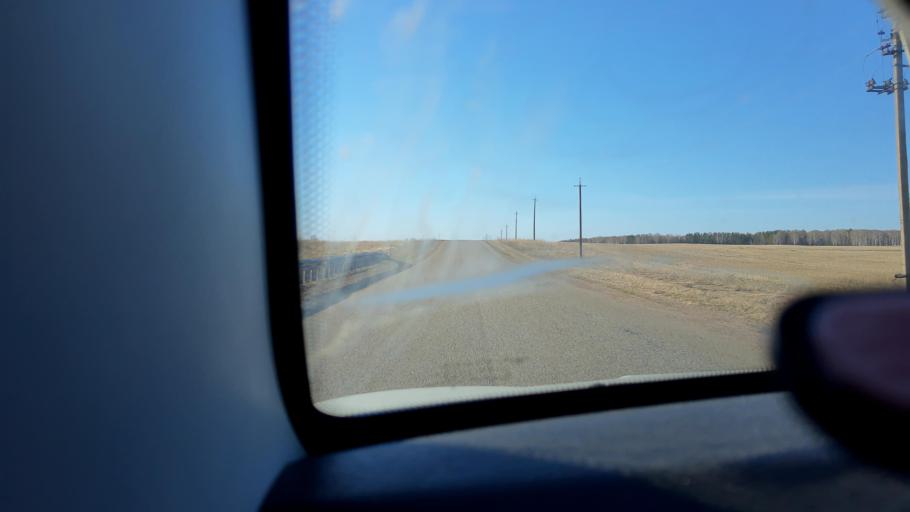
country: RU
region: Bashkortostan
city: Asanovo
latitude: 54.8112
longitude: 55.4826
